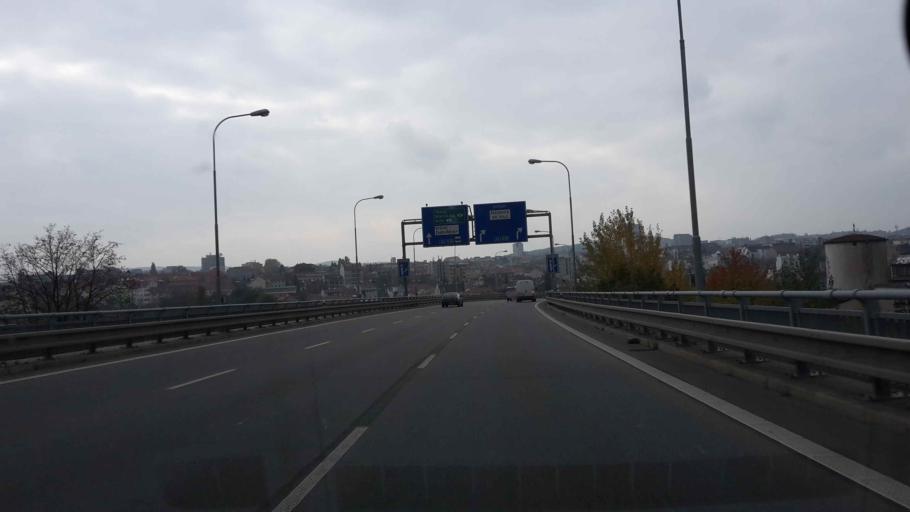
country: CZ
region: South Moravian
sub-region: Mesto Brno
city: Brno
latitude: 49.2203
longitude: 16.6069
